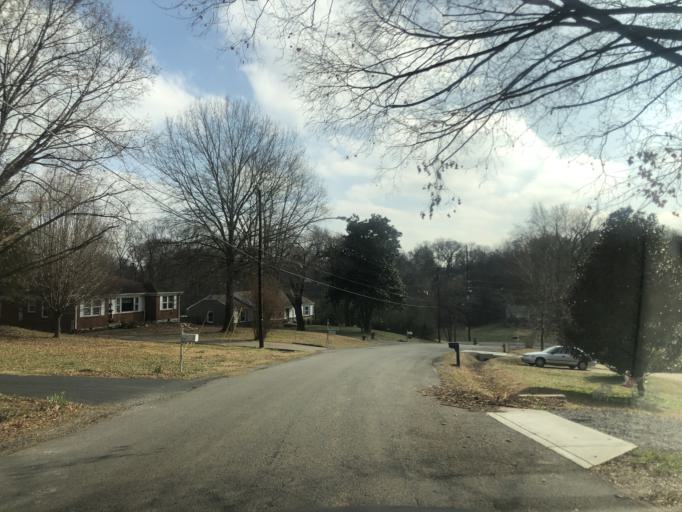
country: US
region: Tennessee
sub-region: Davidson County
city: Oak Hill
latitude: 36.0999
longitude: -86.7200
